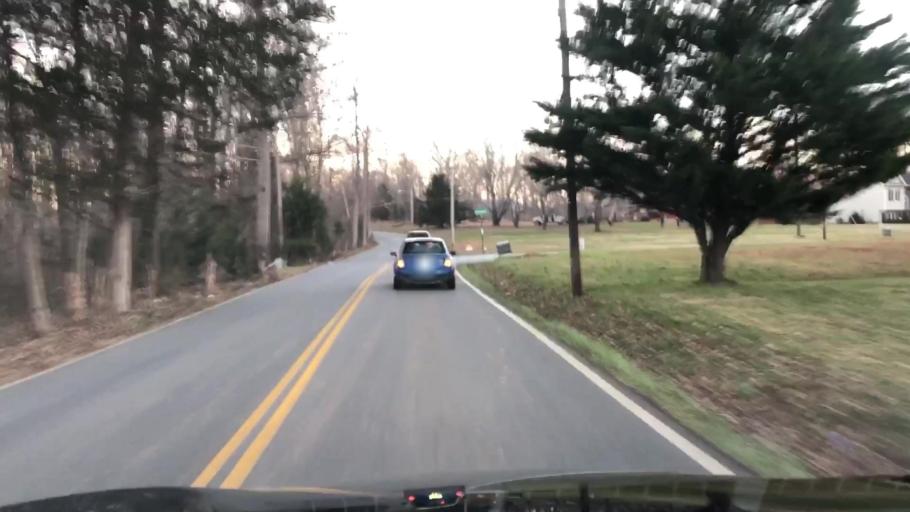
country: US
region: Virginia
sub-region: City of Lynchburg
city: West Lynchburg
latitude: 37.4188
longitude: -79.2390
